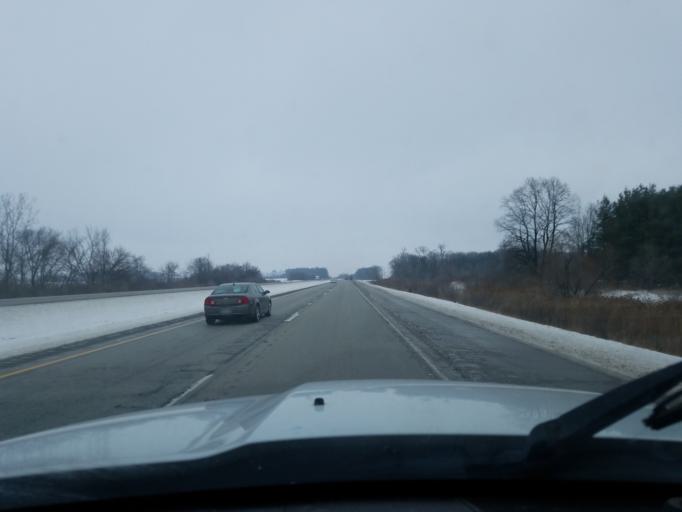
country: US
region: Indiana
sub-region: Marshall County
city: Argos
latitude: 41.1530
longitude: -86.2397
